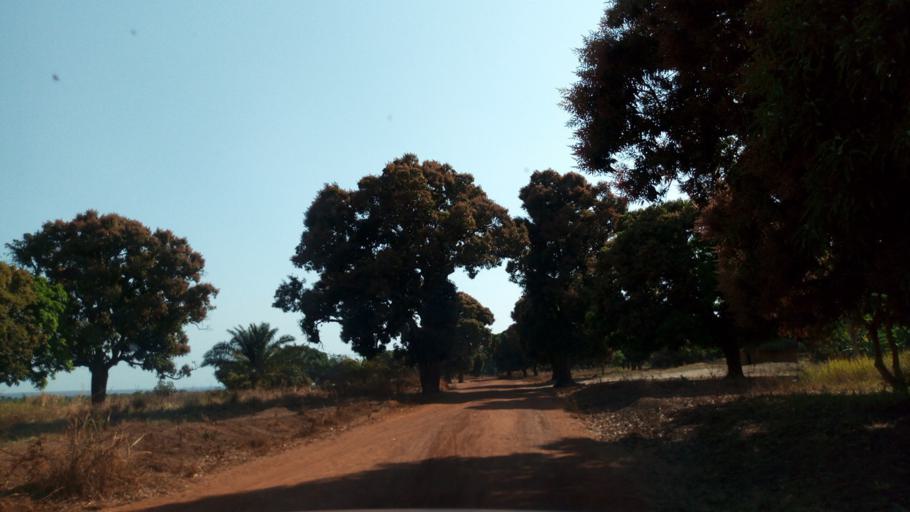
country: ZM
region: Luapula
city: Nchelenge
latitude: -9.1881
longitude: 28.2818
